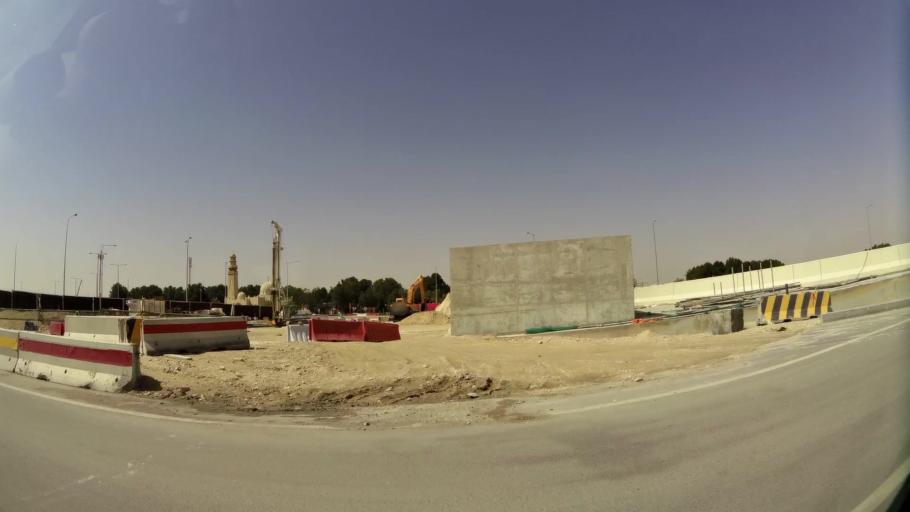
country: QA
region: Baladiyat ad Dawhah
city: Doha
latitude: 25.3743
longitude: 51.5238
